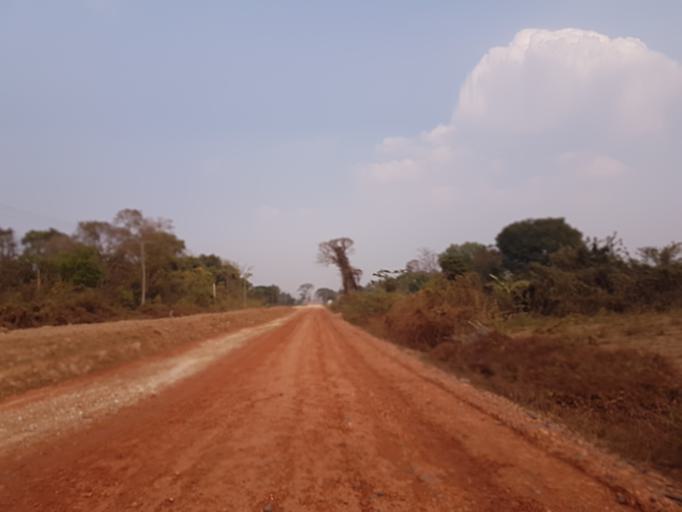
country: TH
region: Nong Khai
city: Nong Khai
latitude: 17.9788
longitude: 102.8716
